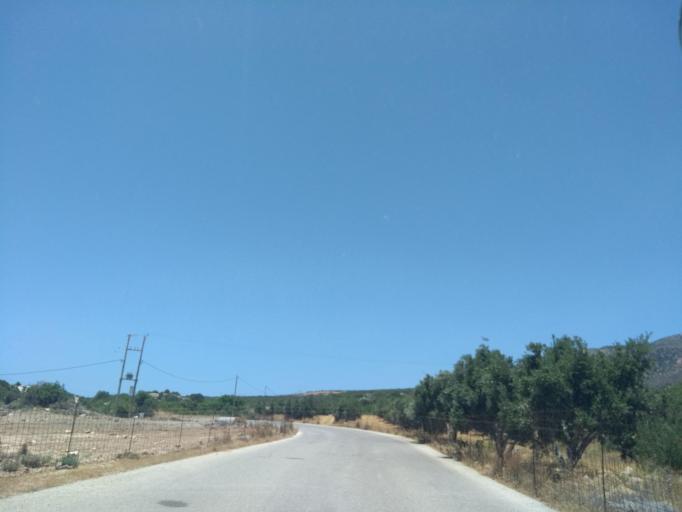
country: GR
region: Crete
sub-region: Nomos Chanias
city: Vryses
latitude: 35.3391
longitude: 23.5448
